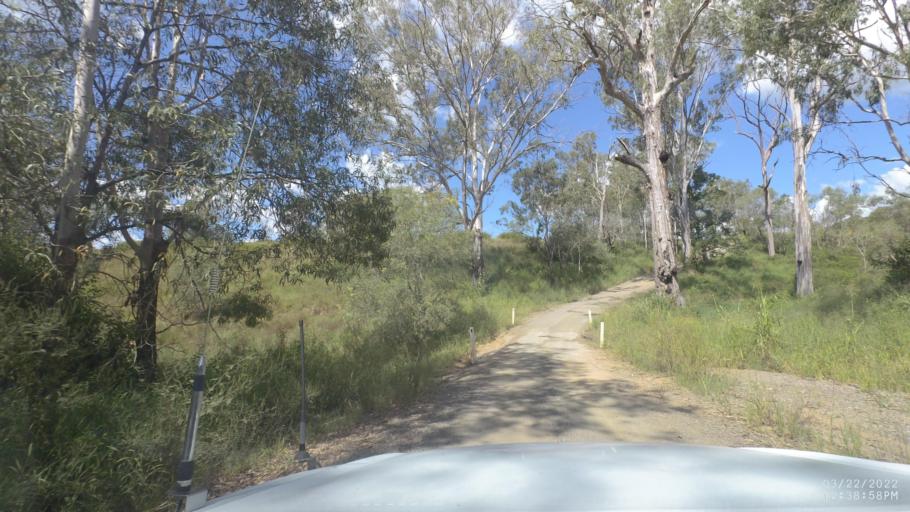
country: AU
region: Queensland
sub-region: Logan
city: North Maclean
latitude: -27.8378
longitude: 152.8738
